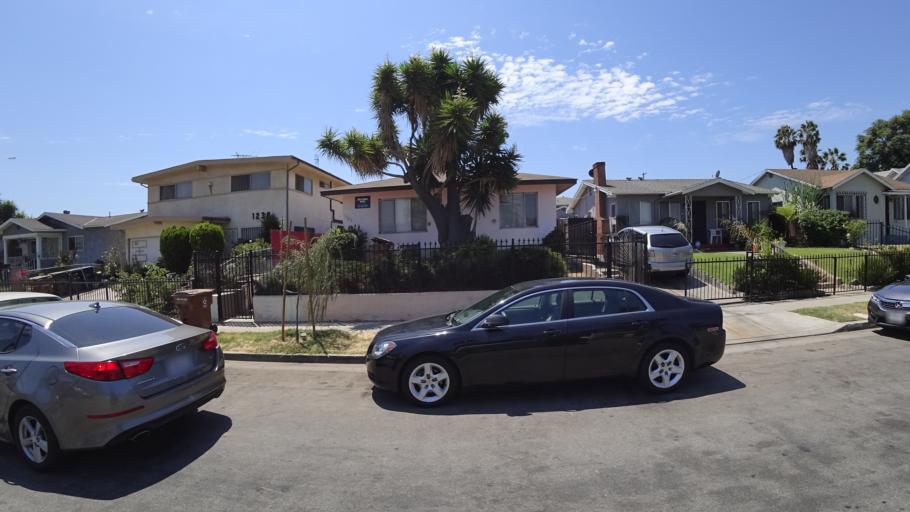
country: US
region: California
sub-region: Los Angeles County
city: Westmont
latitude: 33.9590
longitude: -118.2974
